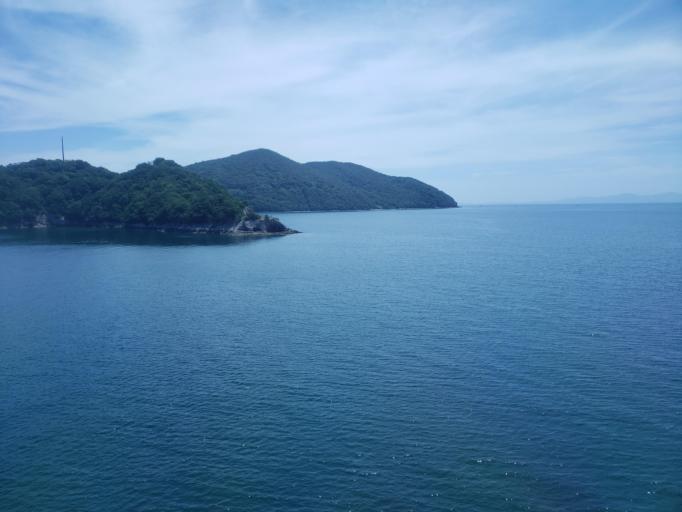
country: JP
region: Kagawa
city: Tonosho
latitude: 34.4467
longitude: 134.3168
